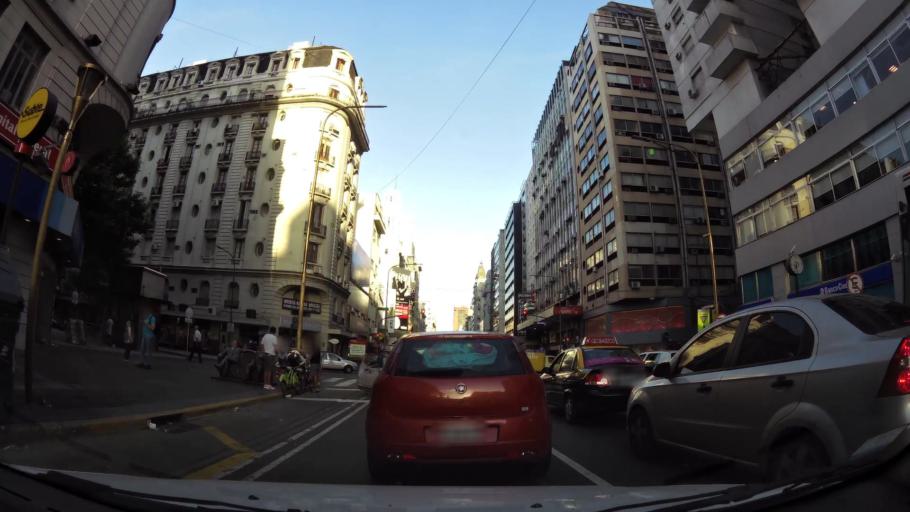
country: AR
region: Buenos Aires F.D.
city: Buenos Aires
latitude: -34.6040
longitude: -58.3869
